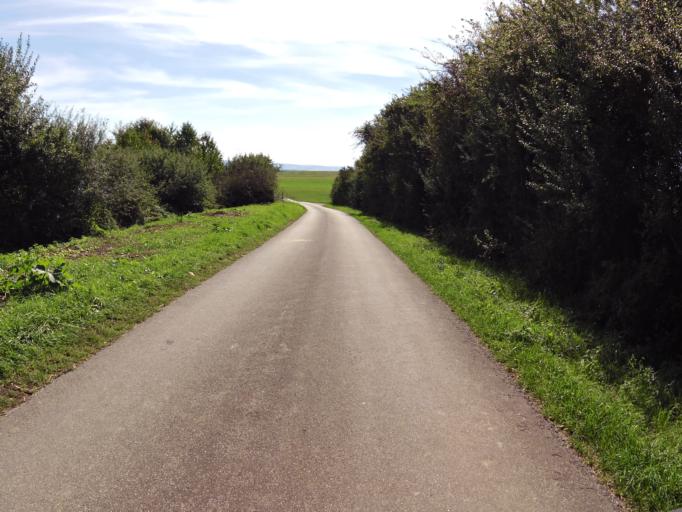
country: DE
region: Baden-Wuerttemberg
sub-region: Freiburg Region
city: Bad Durrheim
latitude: 48.0139
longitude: 8.4977
